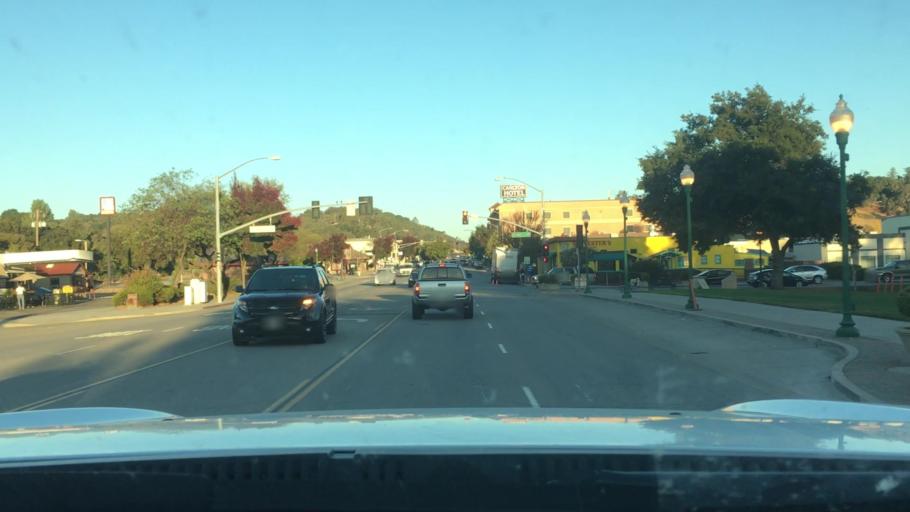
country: US
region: California
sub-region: San Luis Obispo County
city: Atascadero
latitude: 35.4882
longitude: -120.6679
